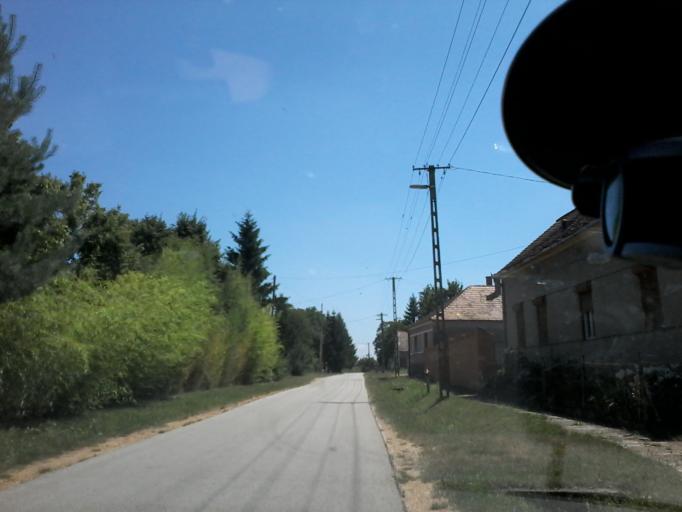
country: HU
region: Vas
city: Janoshaza
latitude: 47.1691
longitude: 17.1173
